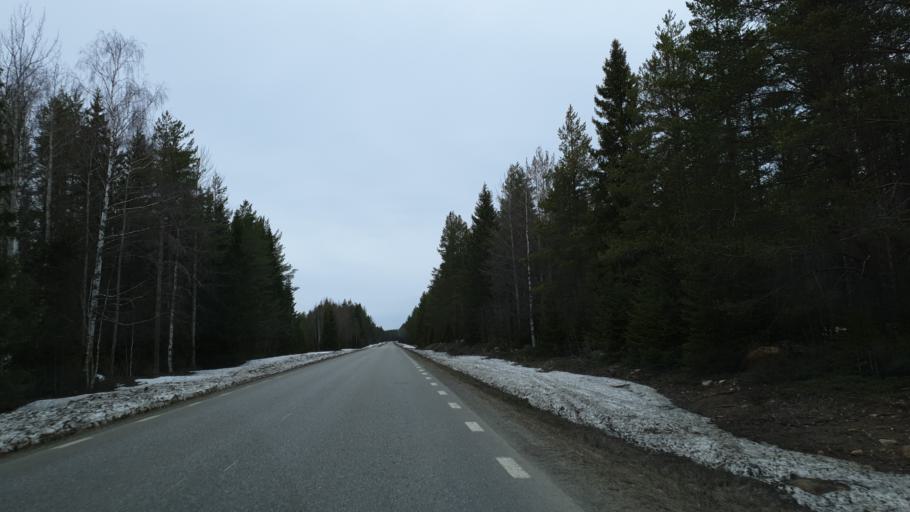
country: SE
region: Vaesterbotten
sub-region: Robertsfors Kommun
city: Robertsfors
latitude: 64.3937
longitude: 20.8928
